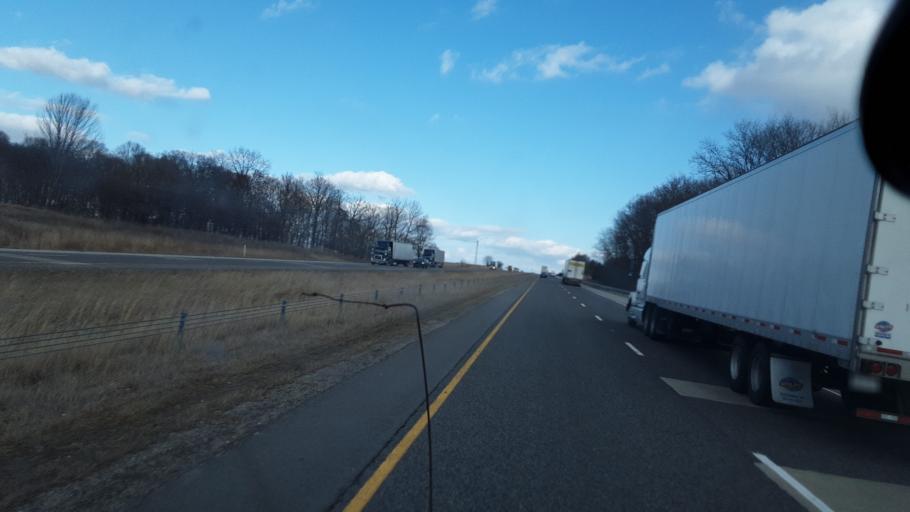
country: US
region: Indiana
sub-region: Wayne County
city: Centerville
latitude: 39.8537
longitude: -85.0625
